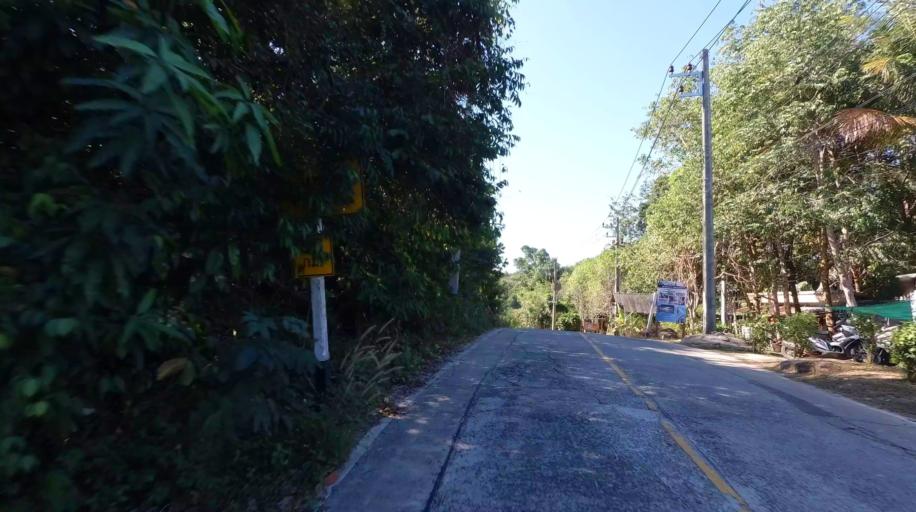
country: TH
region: Trat
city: Ko Kut
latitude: 11.6195
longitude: 102.5445
